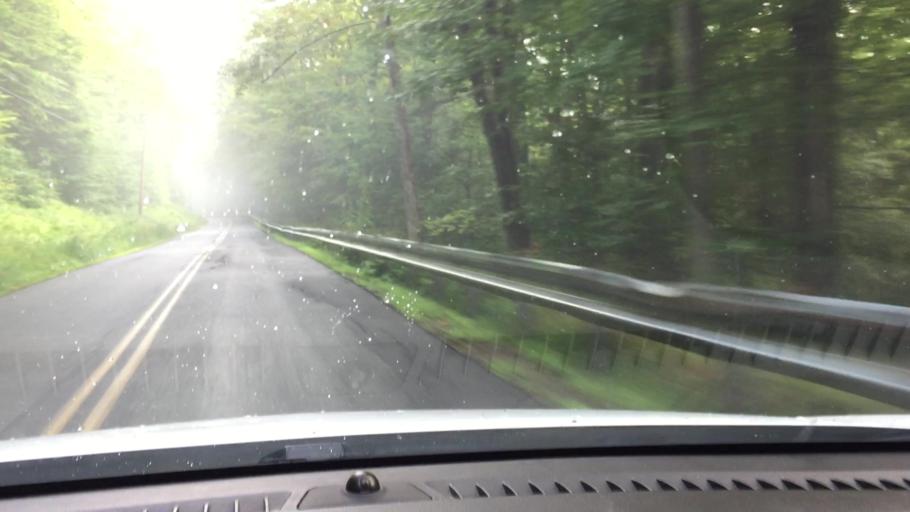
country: US
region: Massachusetts
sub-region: Berkshire County
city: Becket
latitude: 42.4141
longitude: -72.9817
